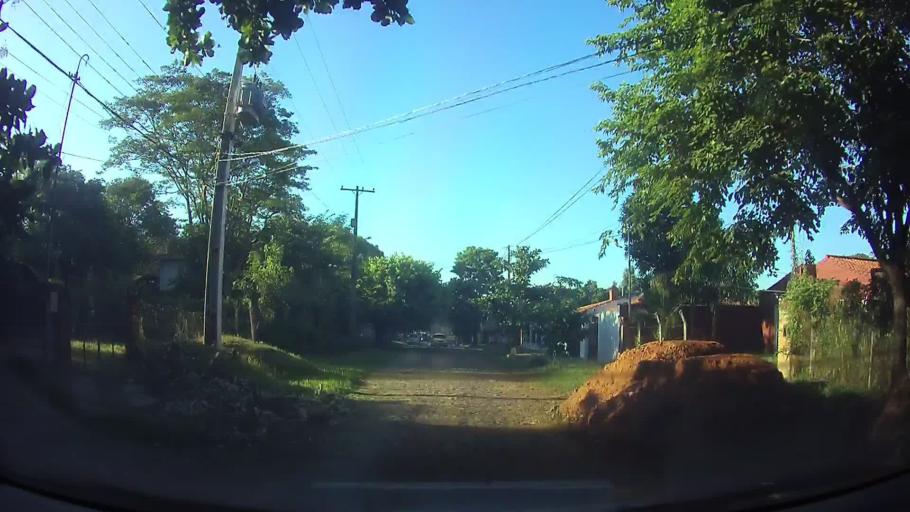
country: PY
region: Central
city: San Lorenzo
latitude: -25.2625
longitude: -57.5084
